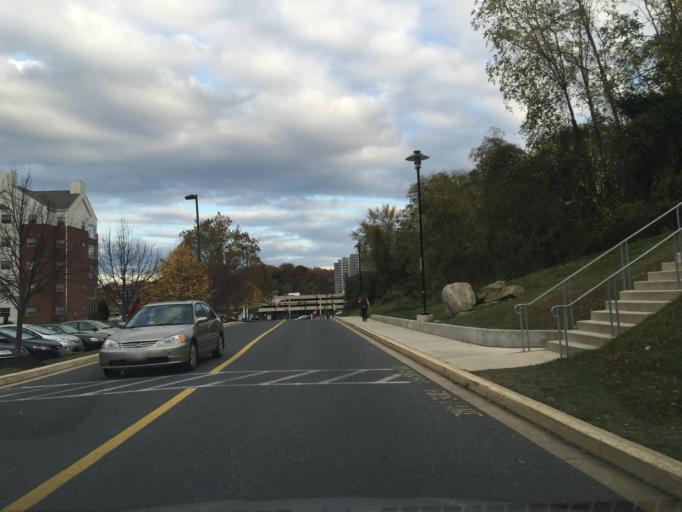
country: US
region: Maryland
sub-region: Baltimore County
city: Towson
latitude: 39.3936
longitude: -76.6169
